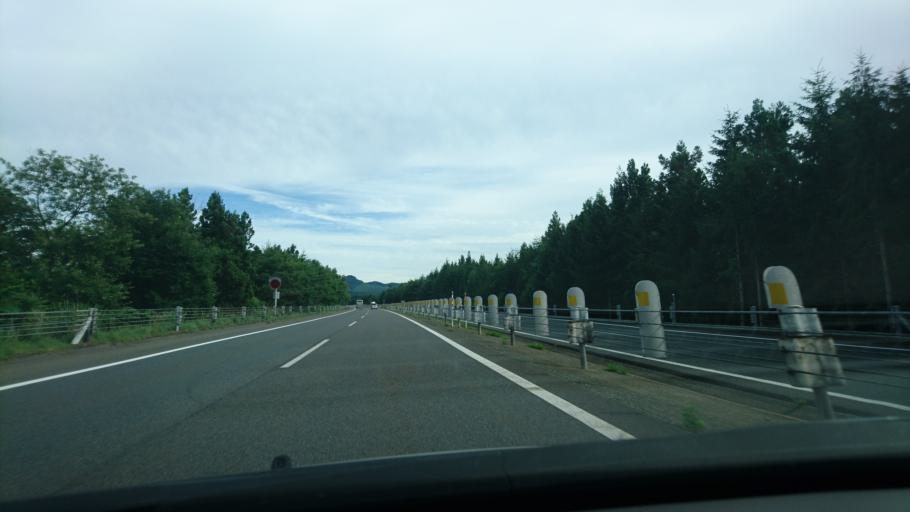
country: JP
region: Iwate
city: Shizukuishi
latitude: 39.9277
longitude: 141.0330
